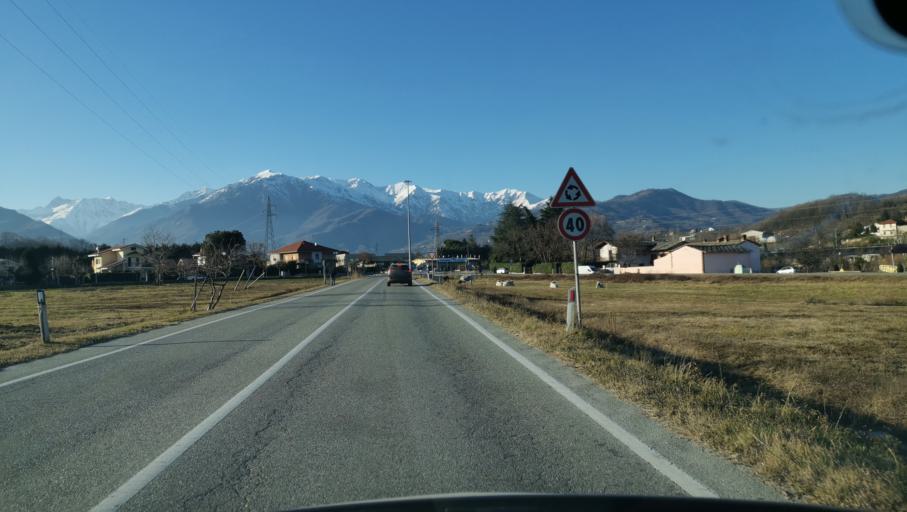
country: IT
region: Piedmont
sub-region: Provincia di Torino
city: Bibiana
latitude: 44.8054
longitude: 7.2896
